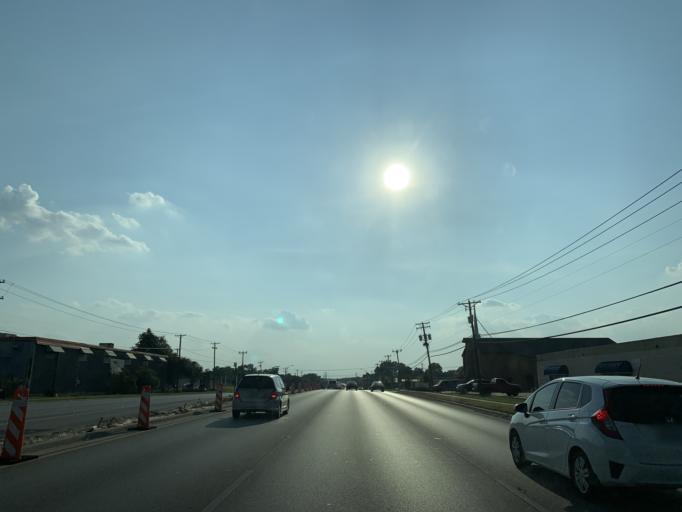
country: US
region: Texas
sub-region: Tarrant County
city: Hurst
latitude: 32.8092
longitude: -97.1840
